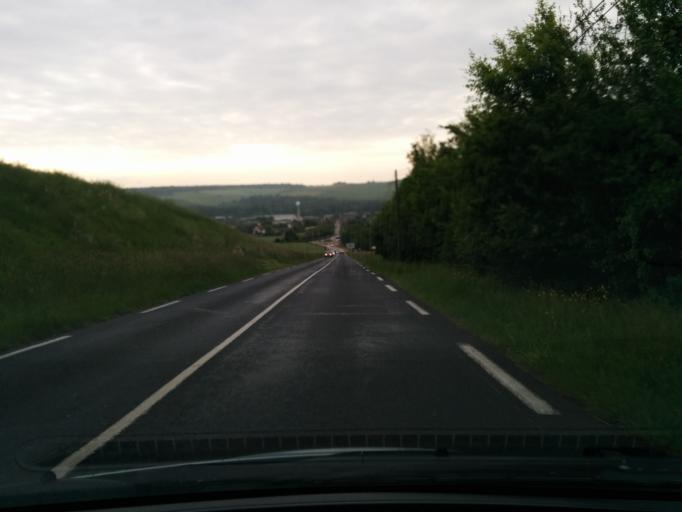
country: FR
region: Haute-Normandie
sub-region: Departement de l'Eure
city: Gasny
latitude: 49.0958
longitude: 1.5897
